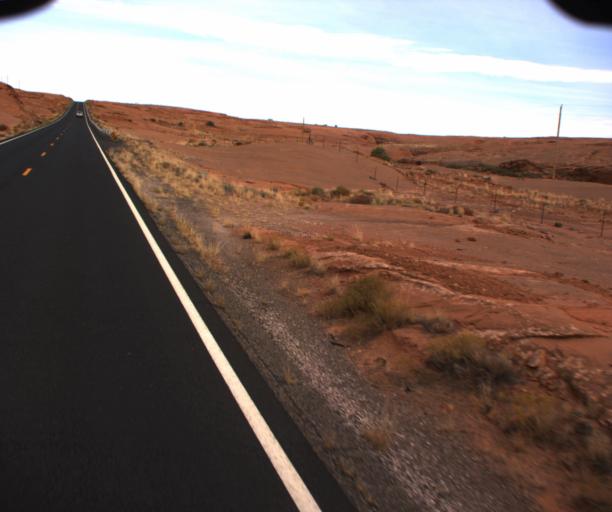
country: US
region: Arizona
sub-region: Apache County
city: Many Farms
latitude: 36.7828
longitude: -109.6565
